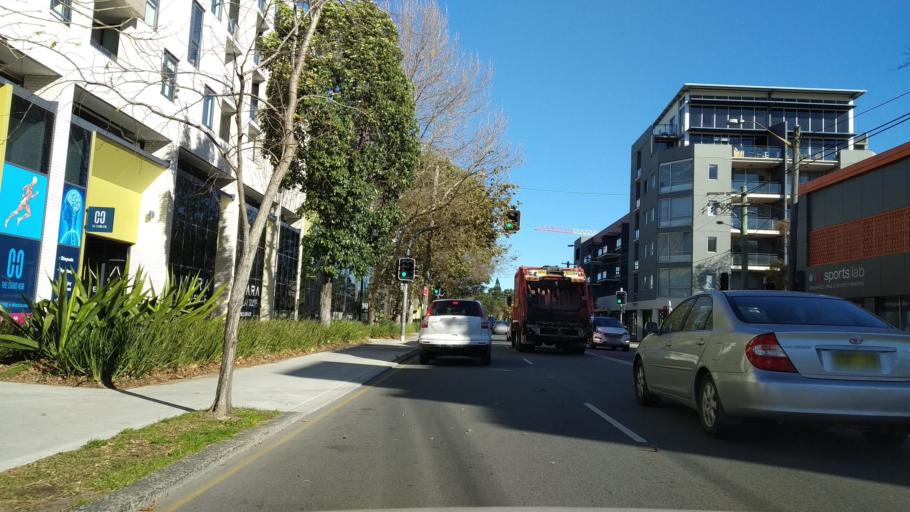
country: AU
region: New South Wales
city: Alexandria
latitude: -33.9183
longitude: 151.1992
